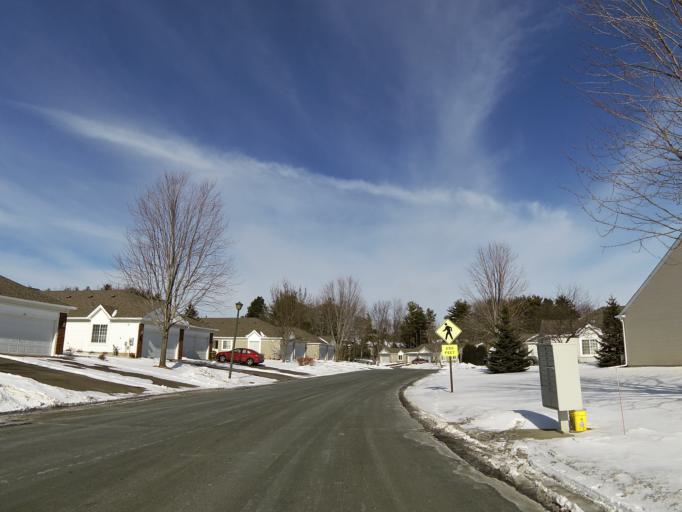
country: US
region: Minnesota
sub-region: Washington County
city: Lake Elmo
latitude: 44.9393
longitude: -92.8947
